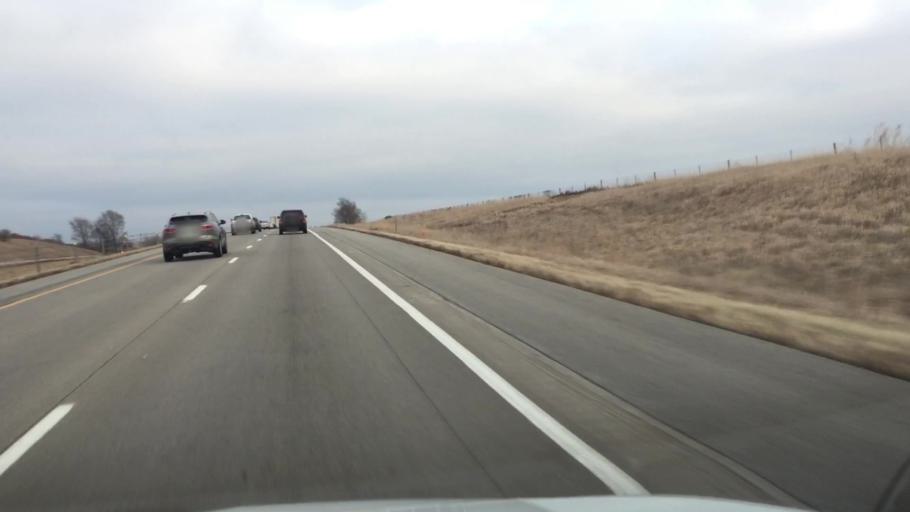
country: US
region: Iowa
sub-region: Jasper County
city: Newton
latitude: 41.6812
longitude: -93.1149
